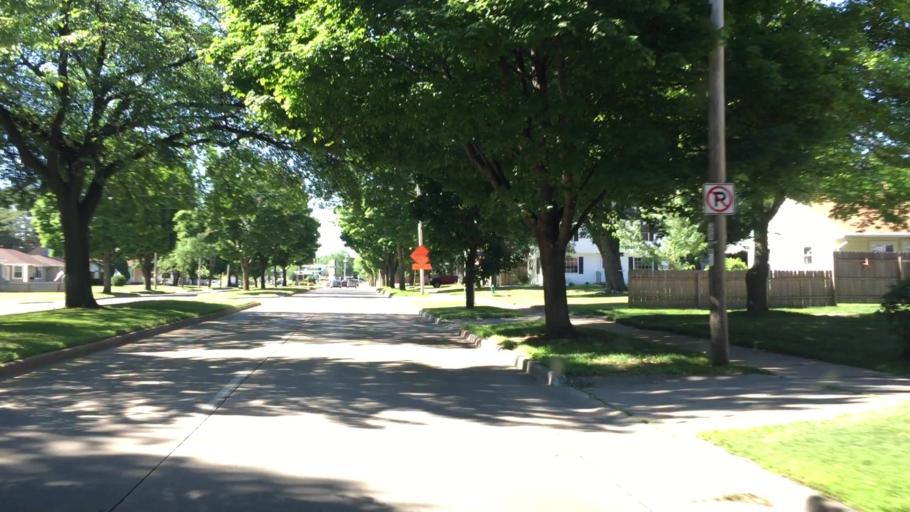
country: US
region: Wisconsin
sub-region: Outagamie County
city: Appleton
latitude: 44.2458
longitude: -88.4157
